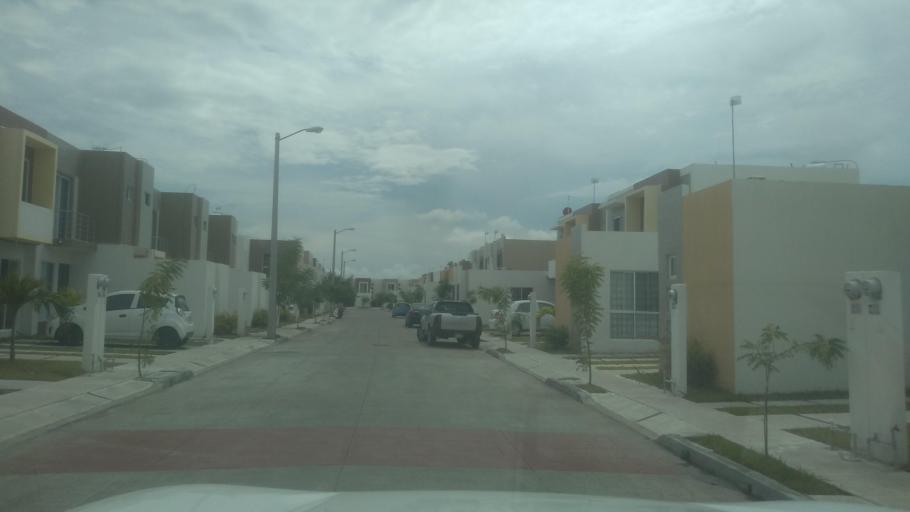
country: MX
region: Veracruz
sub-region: Medellin
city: Fraccionamiento Arboledas San Ramon
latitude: 19.1052
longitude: -96.1648
